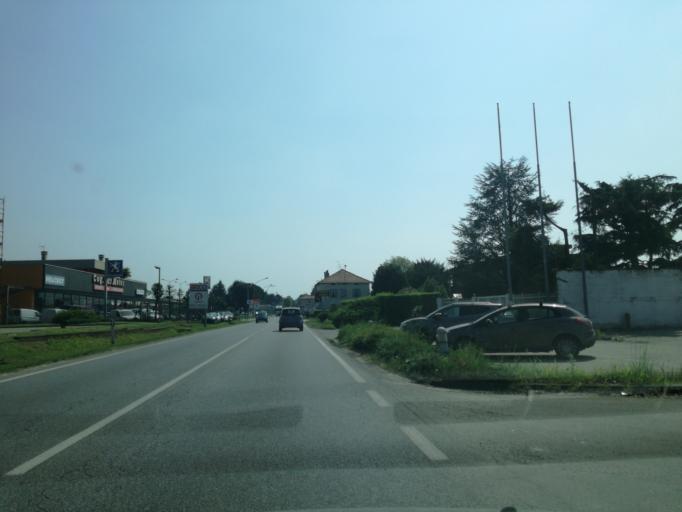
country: IT
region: Lombardy
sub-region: Provincia di Lecco
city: Merate
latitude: 45.6875
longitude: 9.4260
